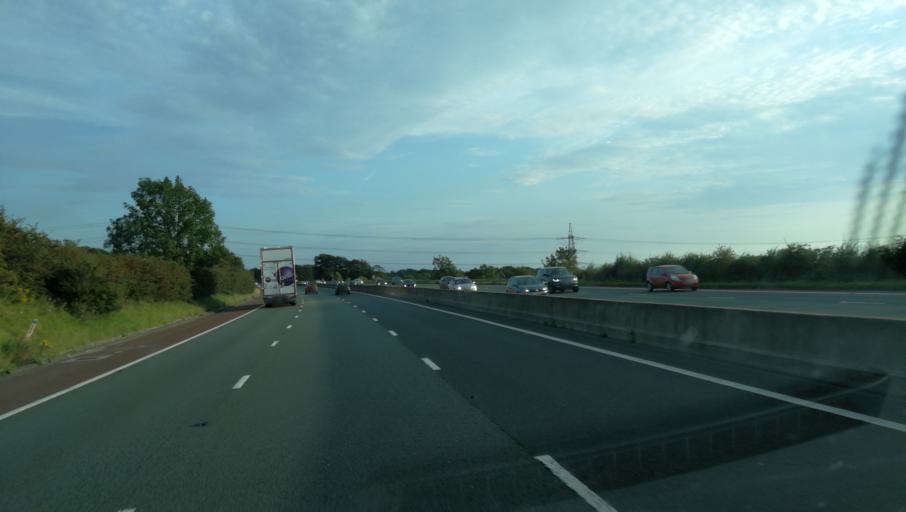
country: GB
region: England
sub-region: Lancashire
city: Lancaster
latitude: 54.0234
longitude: -2.7829
